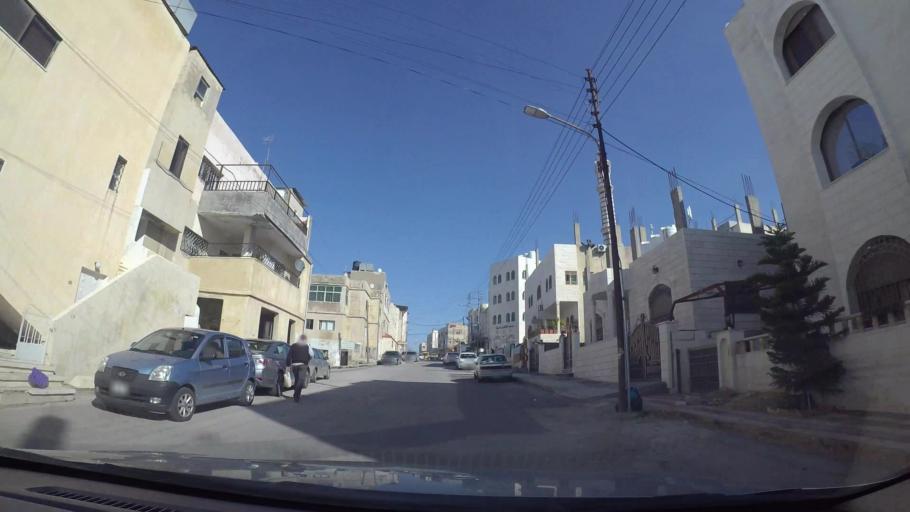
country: JO
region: Amman
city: Al Bunayyat ash Shamaliyah
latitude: 31.9073
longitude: 35.9145
